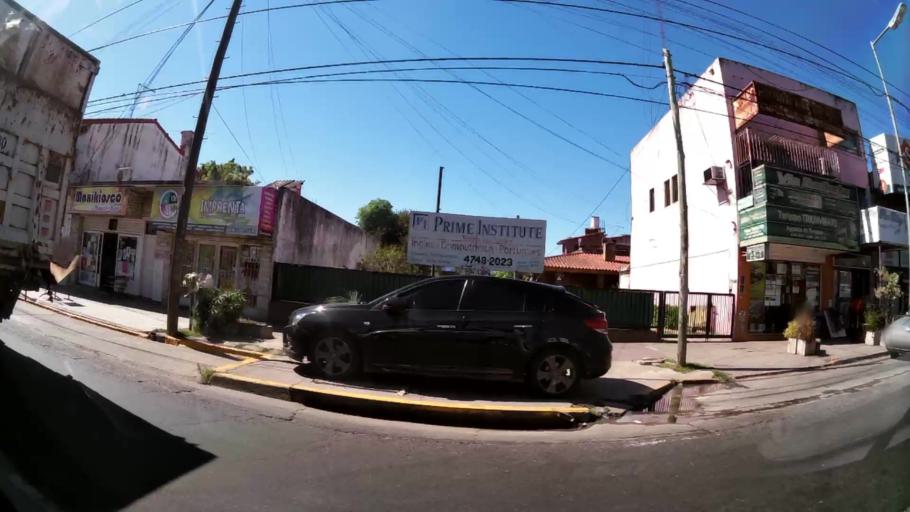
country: AR
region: Buenos Aires
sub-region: Partido de Tigre
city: Tigre
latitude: -34.4869
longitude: -58.6177
